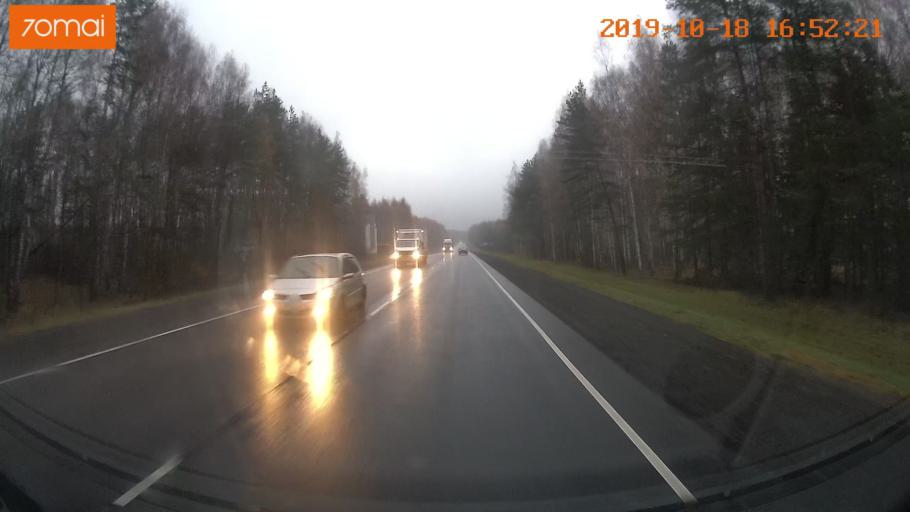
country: RU
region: Ivanovo
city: Nerl'
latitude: 56.5994
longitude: 40.5558
